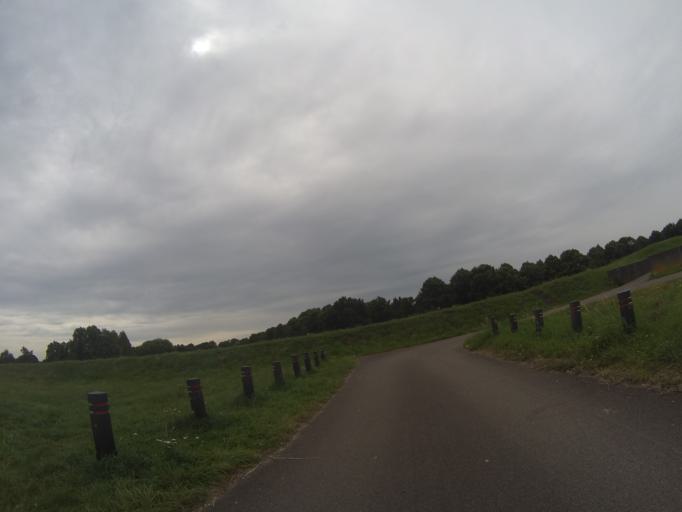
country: NL
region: North Holland
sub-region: Gemeente Naarden
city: Naarden
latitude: 52.2948
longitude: 5.1572
